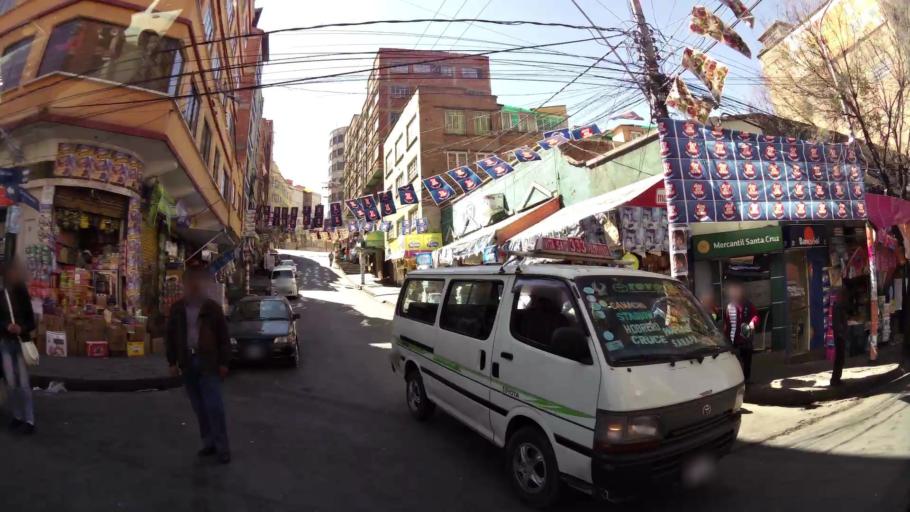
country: BO
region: La Paz
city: La Paz
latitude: -16.4934
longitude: -68.1427
